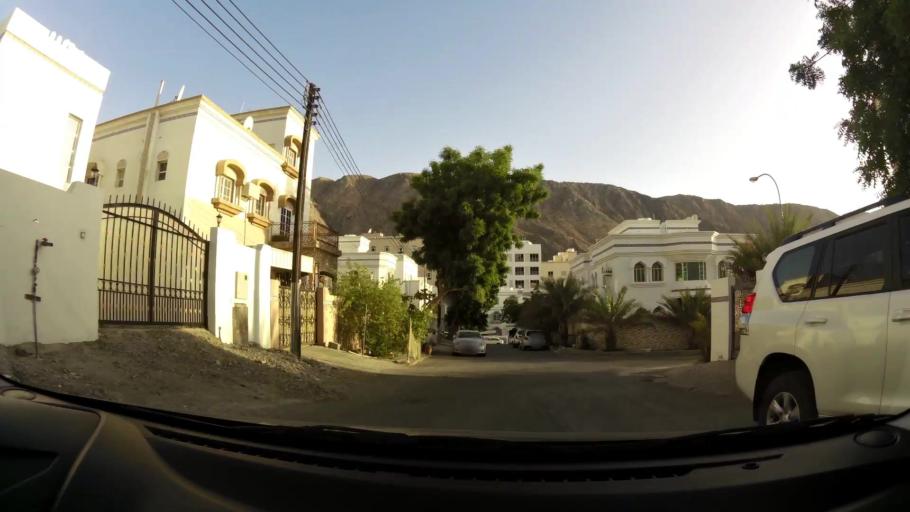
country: OM
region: Muhafazat Masqat
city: Muscat
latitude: 23.5654
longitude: 58.5825
